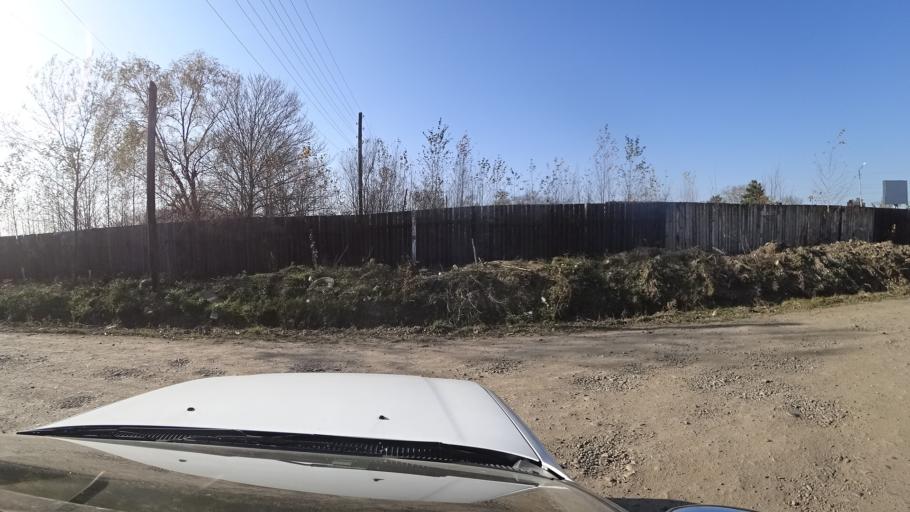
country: RU
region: Primorskiy
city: Dal'nerechensk
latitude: 45.9225
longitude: 133.7461
